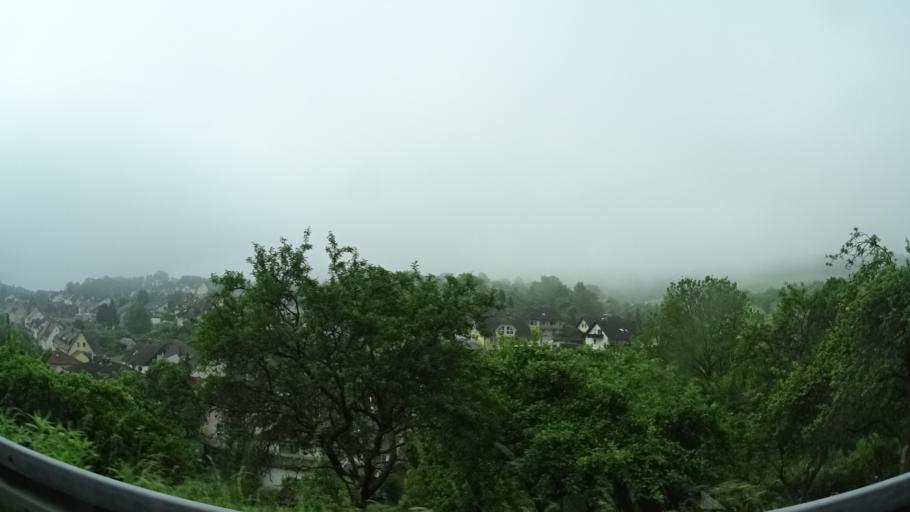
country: DE
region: Bavaria
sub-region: Regierungsbezirk Unterfranken
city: Laudenbach
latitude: 49.7454
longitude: 9.1673
